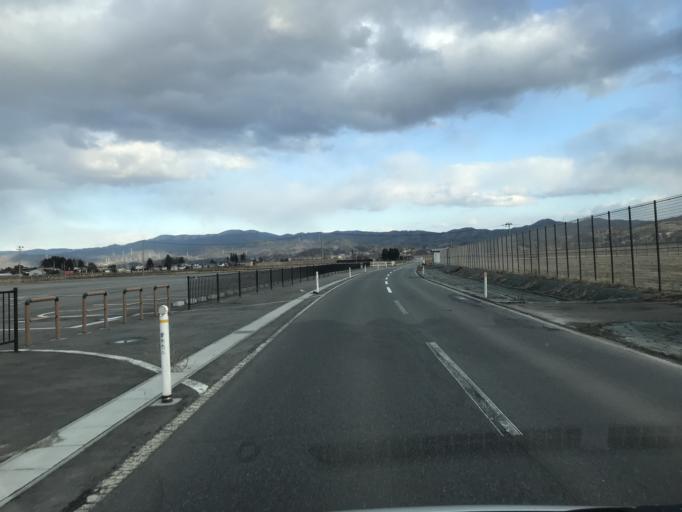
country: JP
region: Iwate
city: Mizusawa
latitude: 39.0582
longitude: 141.1430
